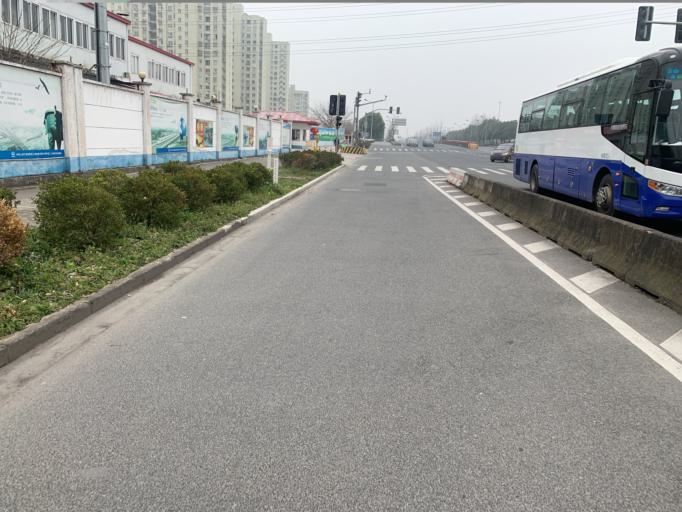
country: CN
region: Shanghai Shi
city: Huamu
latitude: 31.2449
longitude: 121.6212
